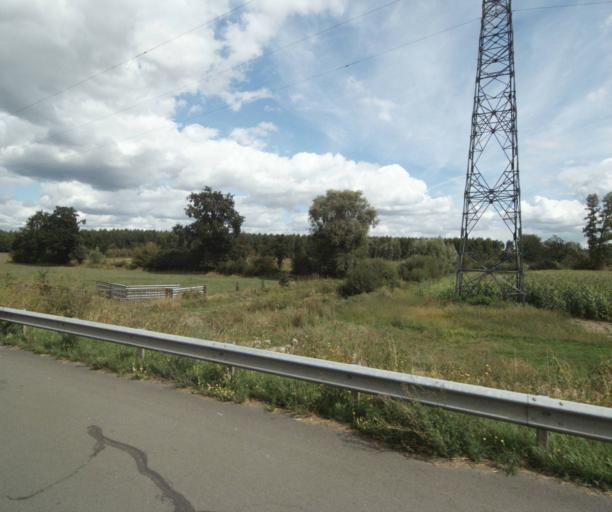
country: FR
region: Nord-Pas-de-Calais
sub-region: Departement du Nord
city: Genech
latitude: 50.5405
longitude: 3.1963
